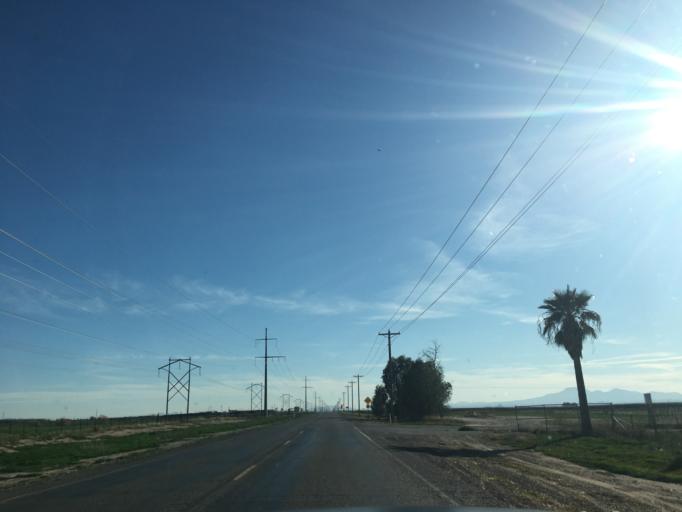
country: US
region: Arizona
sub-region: Pinal County
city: Maricopa
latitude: 33.0197
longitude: -111.9966
